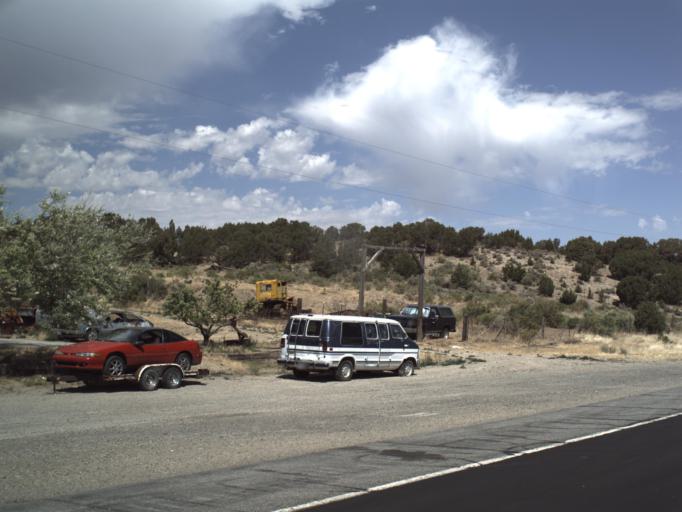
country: US
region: Utah
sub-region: Utah County
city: Eagle Mountain
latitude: 40.0143
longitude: -112.2778
